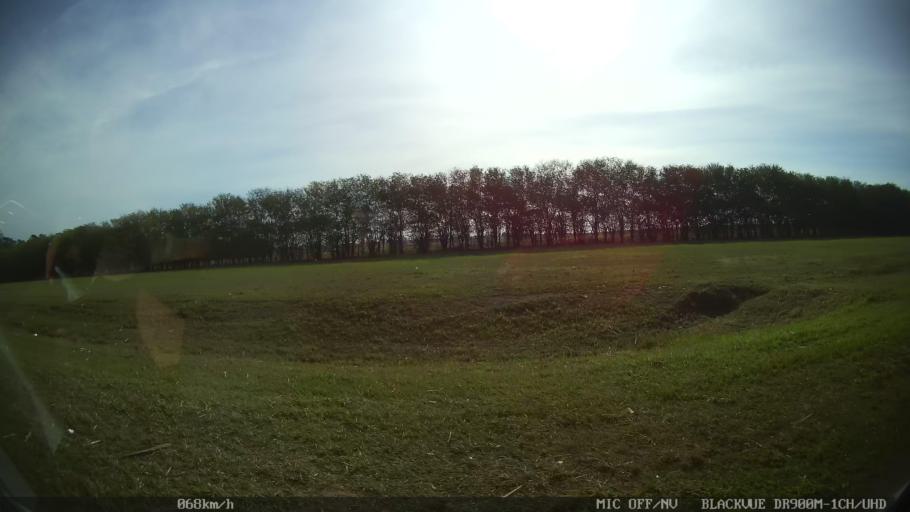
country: BR
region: Sao Paulo
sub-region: Rio Das Pedras
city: Rio das Pedras
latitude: -22.7967
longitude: -47.6102
